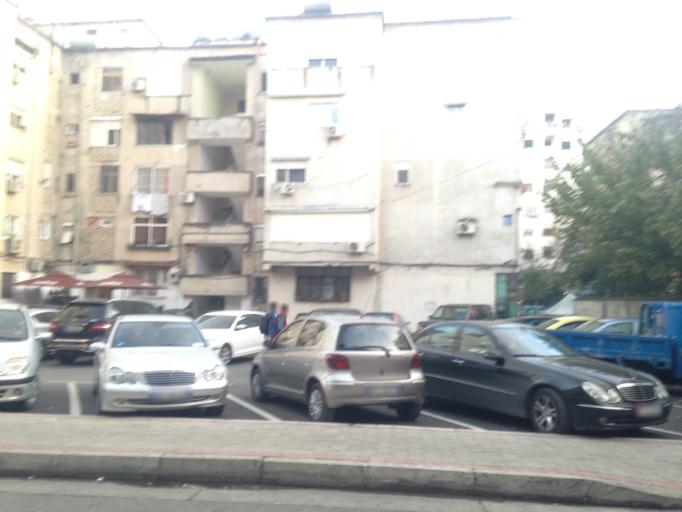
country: AL
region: Tirane
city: Tirana
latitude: 41.3168
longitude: 19.8104
